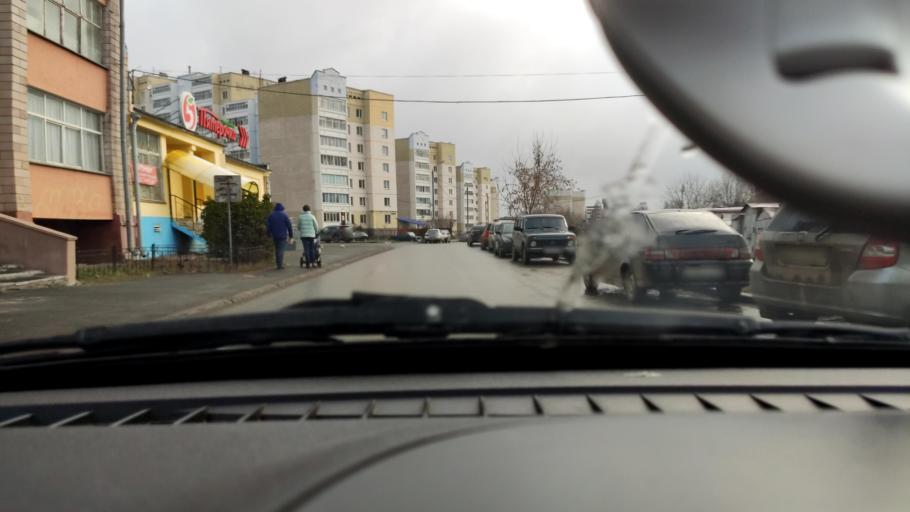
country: RU
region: Perm
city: Kondratovo
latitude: 58.0355
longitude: 56.1326
